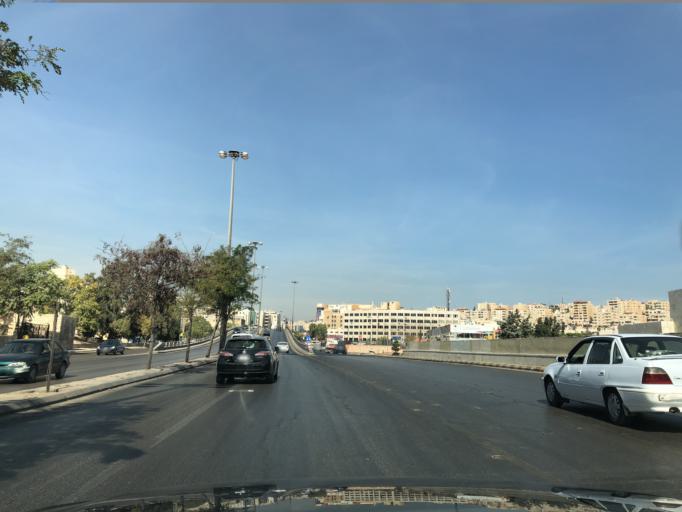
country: JO
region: Amman
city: Amman
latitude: 31.9838
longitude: 35.9003
